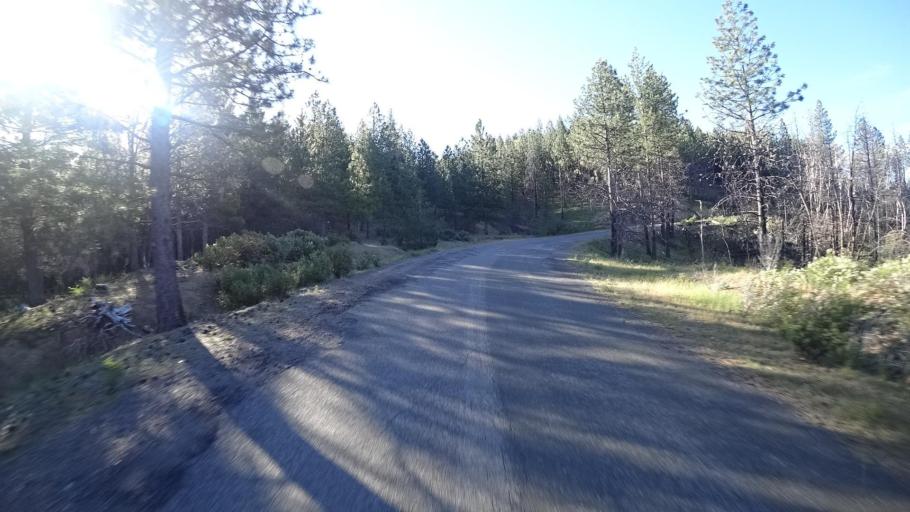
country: US
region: California
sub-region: Lake County
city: Upper Lake
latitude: 39.2973
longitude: -122.9267
